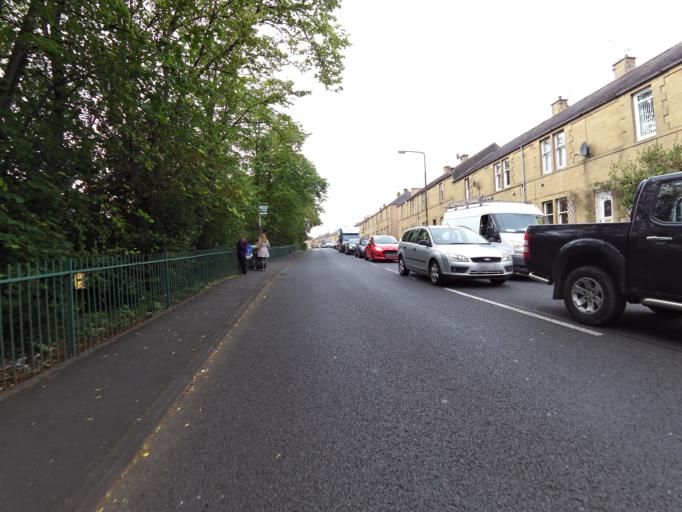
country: GB
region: Scotland
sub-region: East Lothian
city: Musselburgh
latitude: 55.9394
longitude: -3.0610
